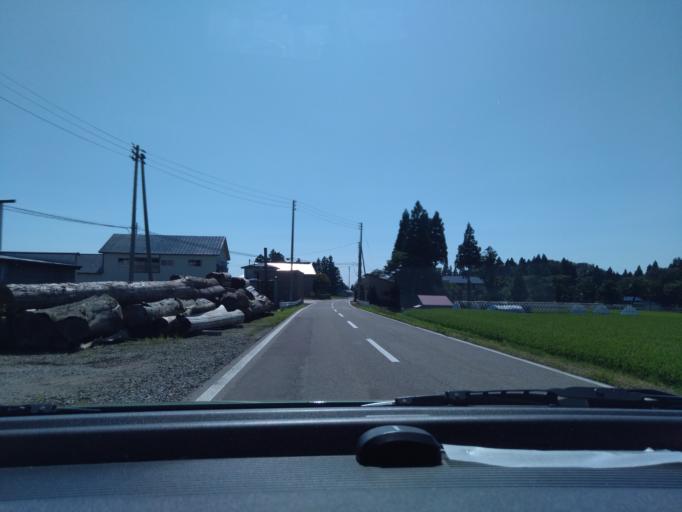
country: JP
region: Akita
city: Kakunodatemachi
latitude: 39.4813
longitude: 140.6169
